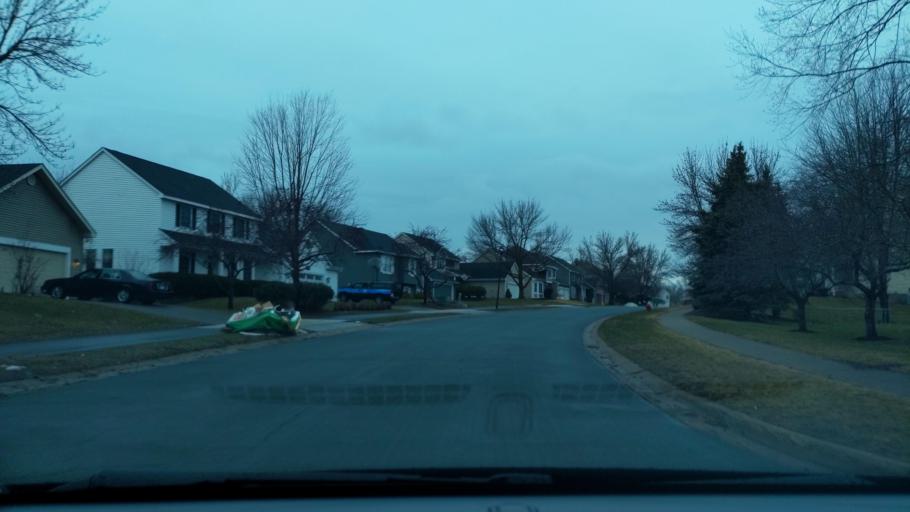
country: US
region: Minnesota
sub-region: Hennepin County
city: Eden Prairie
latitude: 44.8486
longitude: -93.4905
